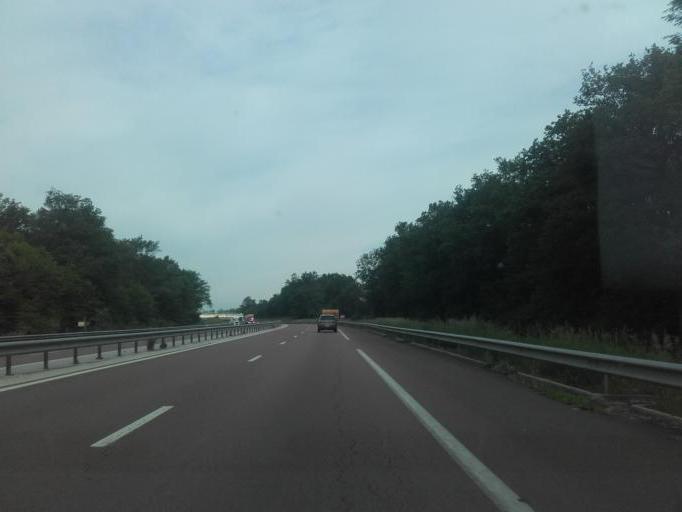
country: FR
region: Bourgogne
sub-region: Departement de Saone-et-Loire
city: Givry
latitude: 46.7602
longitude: 4.7505
